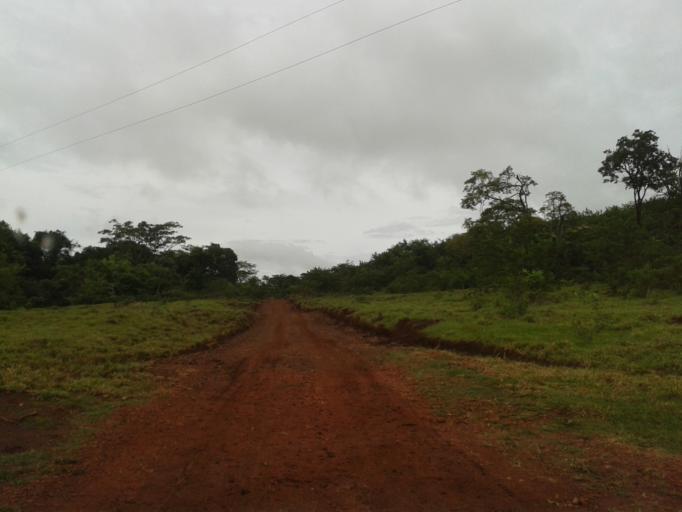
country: BR
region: Minas Gerais
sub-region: Capinopolis
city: Capinopolis
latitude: -18.7361
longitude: -49.7749
